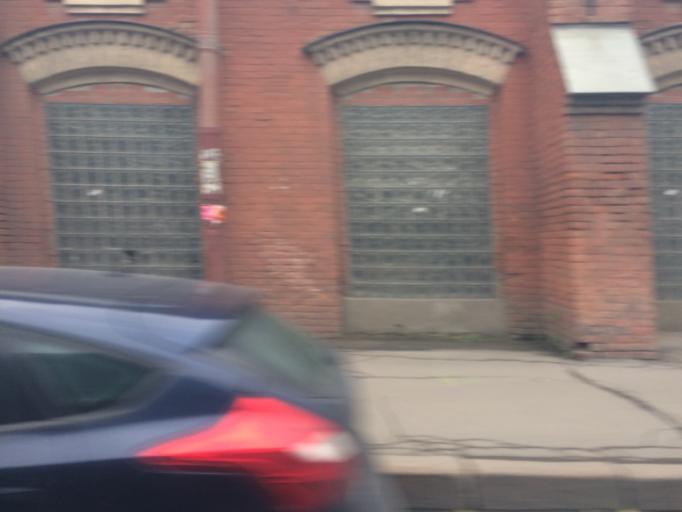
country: RU
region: Leningrad
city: Rybatskoye
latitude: 59.8618
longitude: 30.4773
